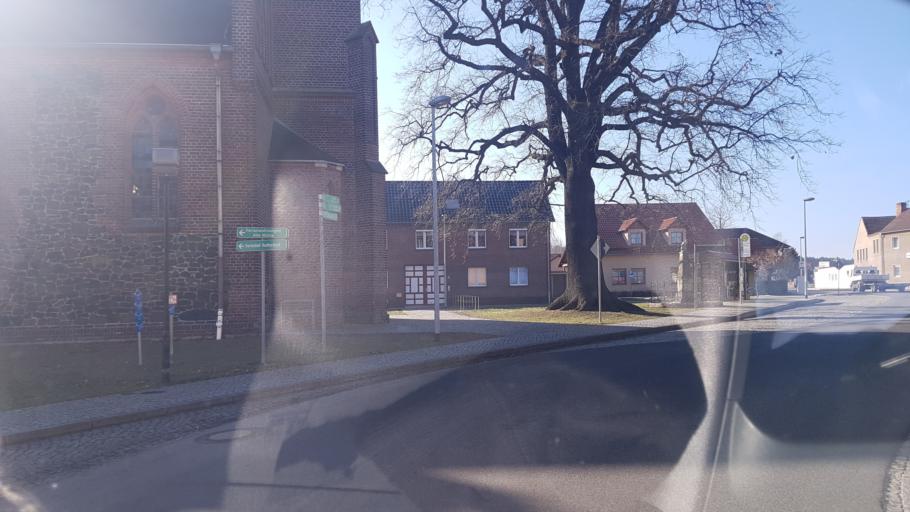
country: DE
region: Brandenburg
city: Senftenberg
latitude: 51.4962
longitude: 14.0600
